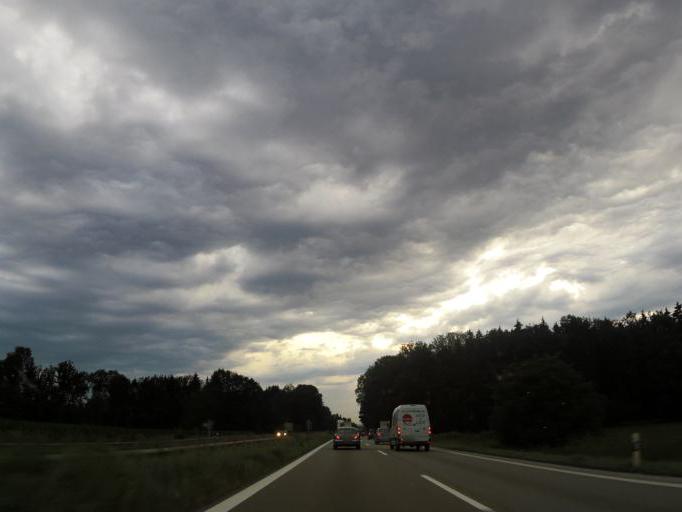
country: DE
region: Bavaria
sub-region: Upper Bavaria
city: Rohrdorf
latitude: 47.8053
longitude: 12.1476
